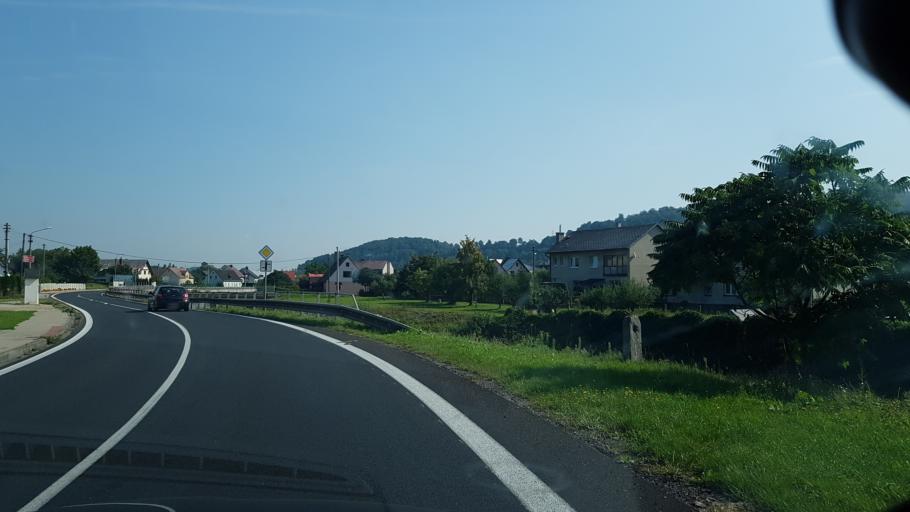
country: CZ
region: Olomoucky
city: Ceska Ves
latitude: 50.2600
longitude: 17.2344
